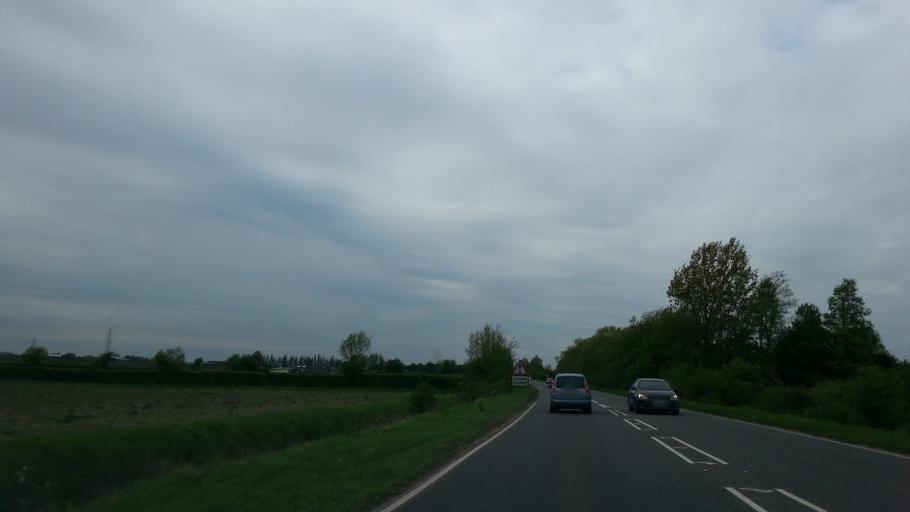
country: GB
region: England
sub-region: Cambridgeshire
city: March
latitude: 52.5470
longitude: 0.0703
